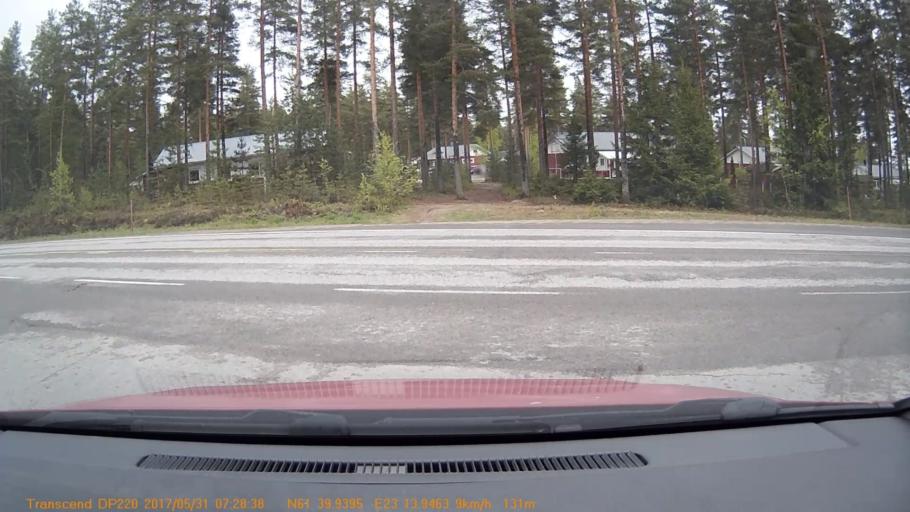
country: FI
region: Pirkanmaa
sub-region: Tampere
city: Haemeenkyroe
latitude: 61.6657
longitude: 23.2324
